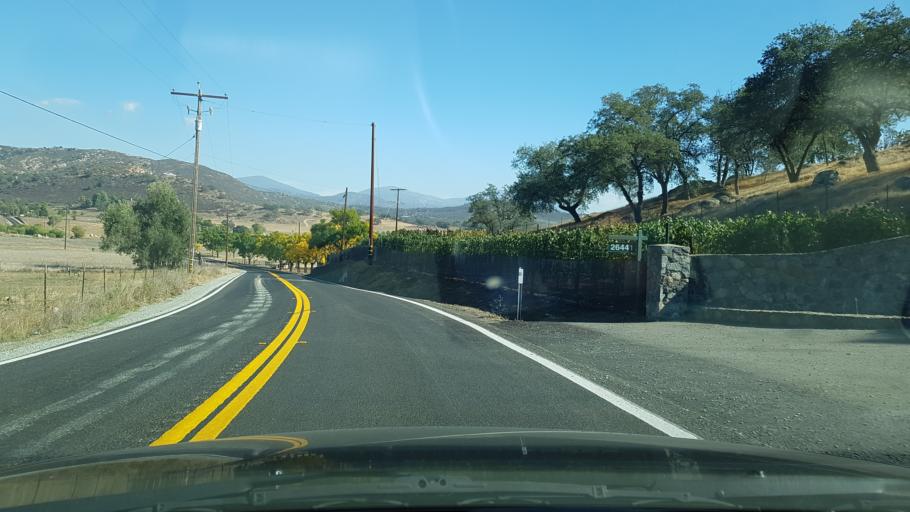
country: US
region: California
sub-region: San Diego County
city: San Diego Country Estates
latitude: 33.0660
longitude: -116.7604
